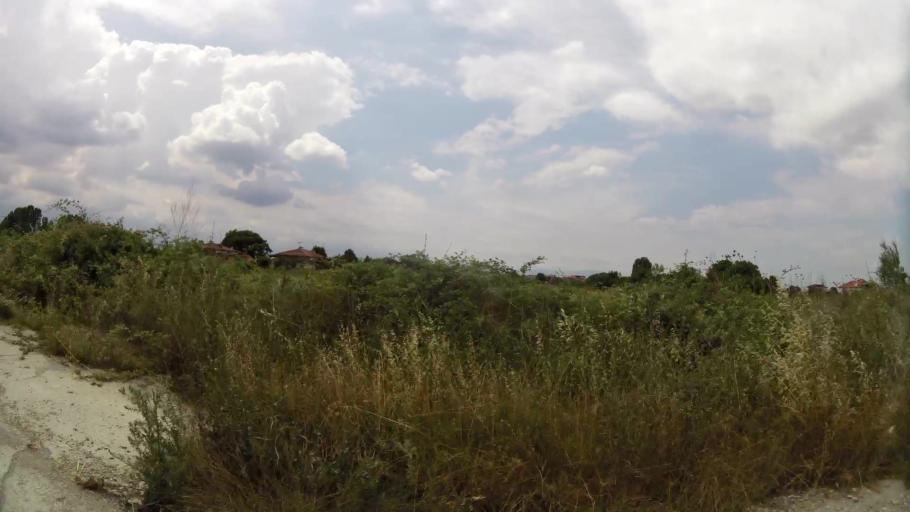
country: GR
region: Central Macedonia
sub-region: Nomos Pierias
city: Paralia
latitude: 40.2733
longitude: 22.5886
